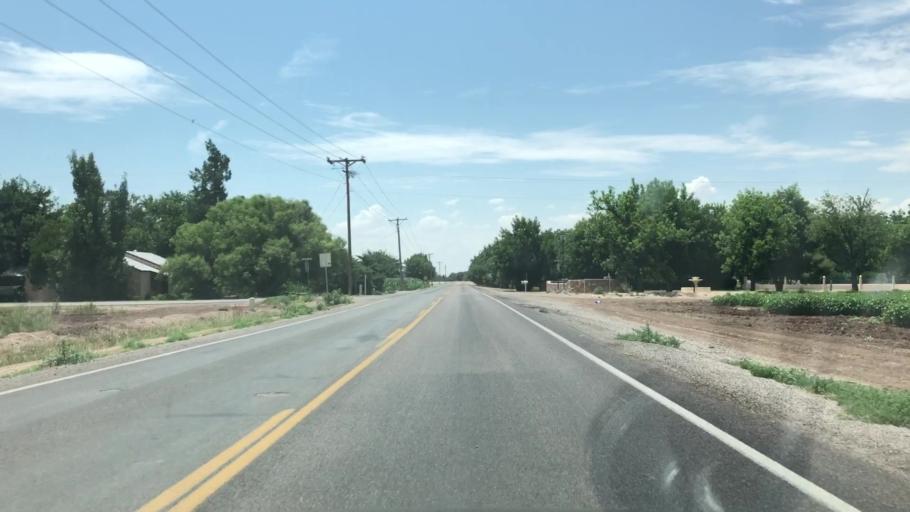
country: US
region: New Mexico
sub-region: Dona Ana County
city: Vado
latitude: 32.0977
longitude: -106.6836
